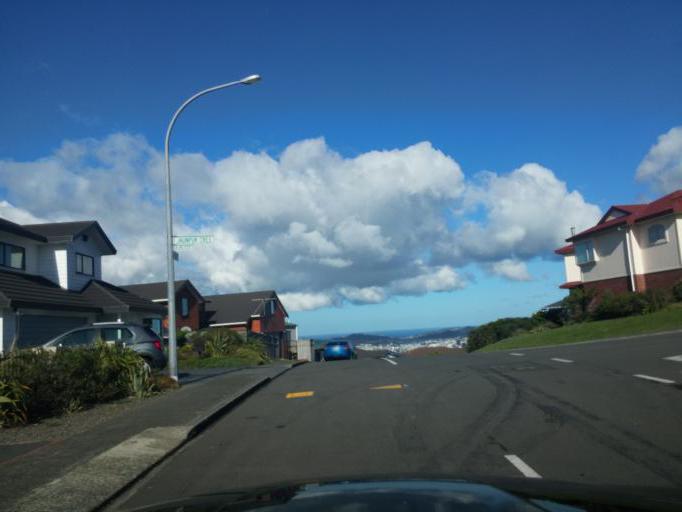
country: NZ
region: Wellington
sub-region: Wellington City
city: Wellington
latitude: -41.2358
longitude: 174.7932
